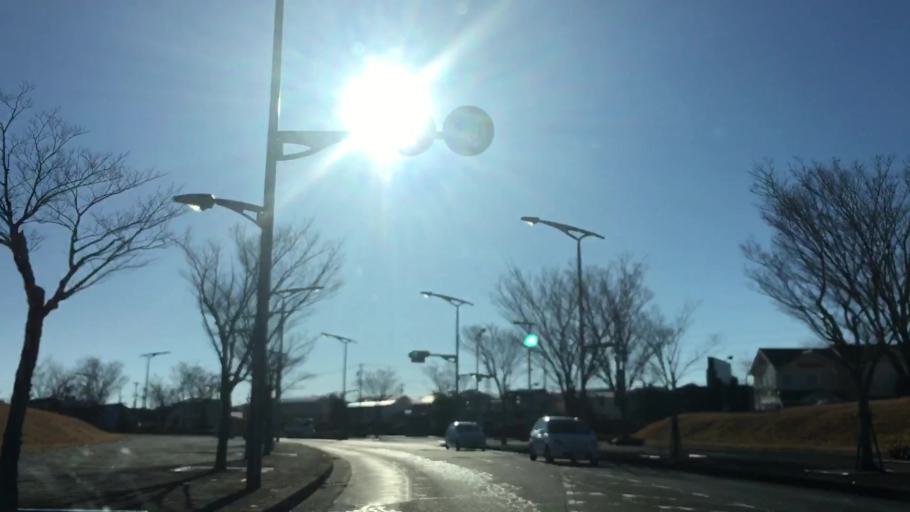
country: JP
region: Shizuoka
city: Hamakita
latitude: 34.8179
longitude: 137.7360
